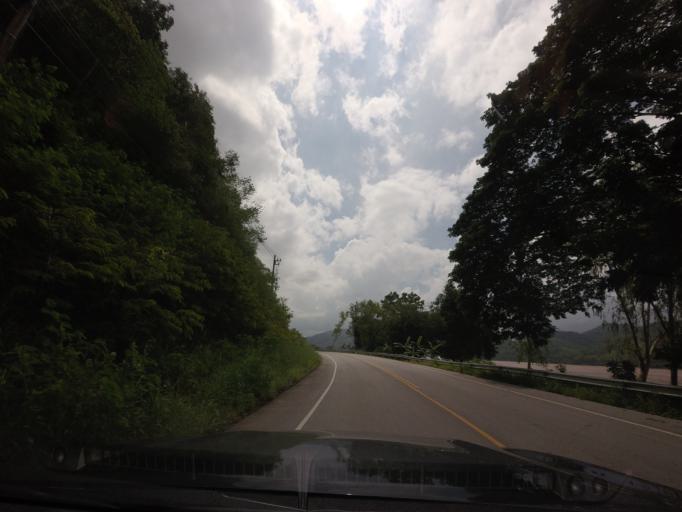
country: TH
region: Loei
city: Pak Chom
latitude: 18.0437
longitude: 101.7711
